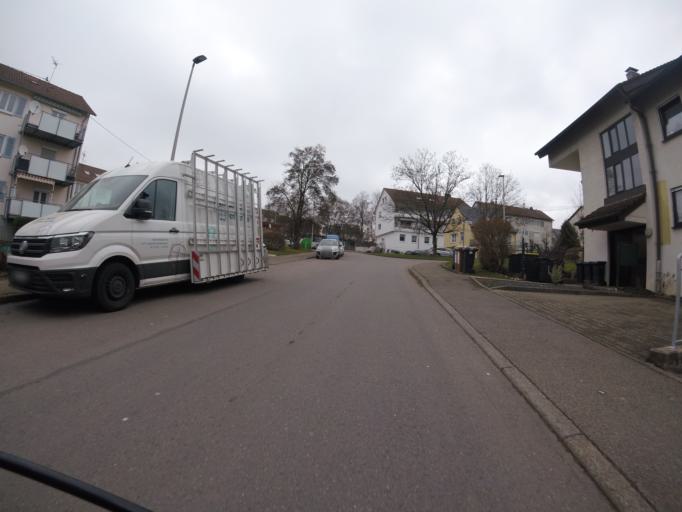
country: DE
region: Baden-Wuerttemberg
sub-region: Regierungsbezirk Stuttgart
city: Backnang
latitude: 48.9502
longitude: 9.4442
